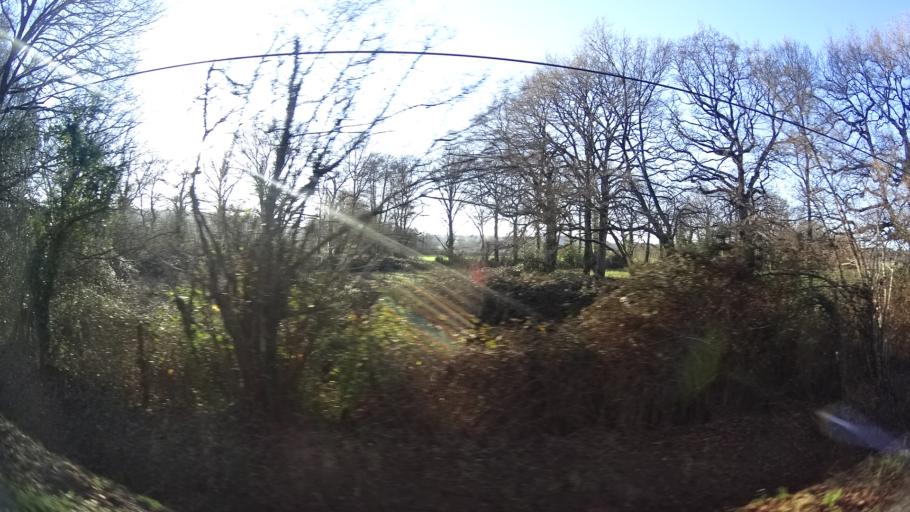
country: FR
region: Brittany
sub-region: Departement du Morbihan
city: Allaire
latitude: 47.6719
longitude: -2.1734
